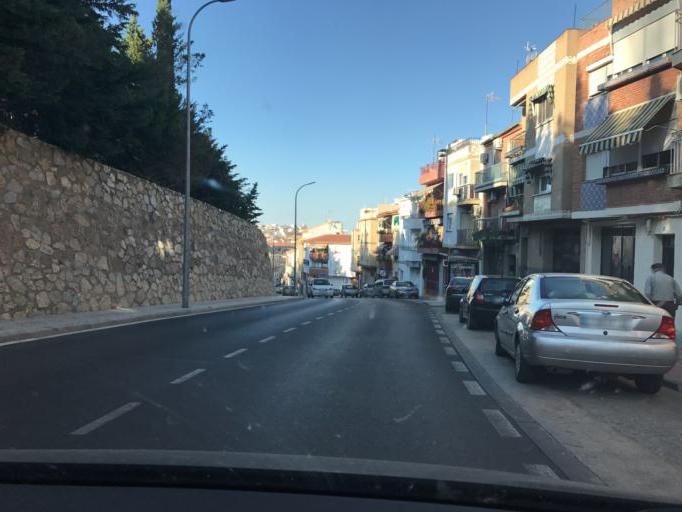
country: ES
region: Andalusia
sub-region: Provincia de Jaen
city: Jaen
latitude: 37.7598
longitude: -3.7912
